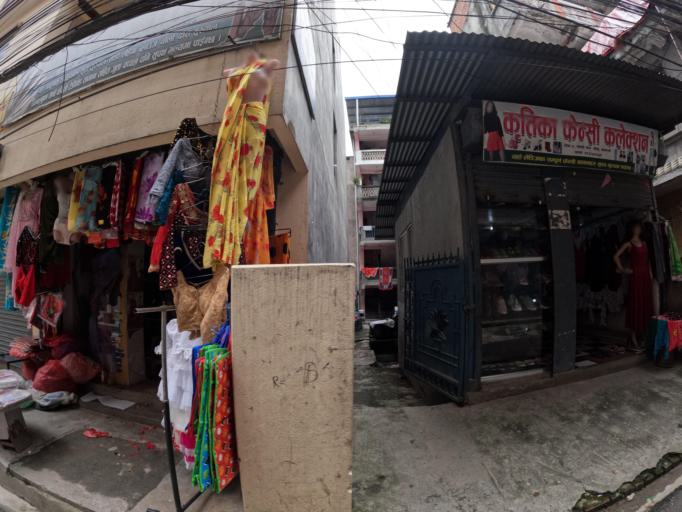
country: NP
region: Central Region
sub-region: Bagmati Zone
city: Kathmandu
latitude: 27.7379
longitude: 85.3121
